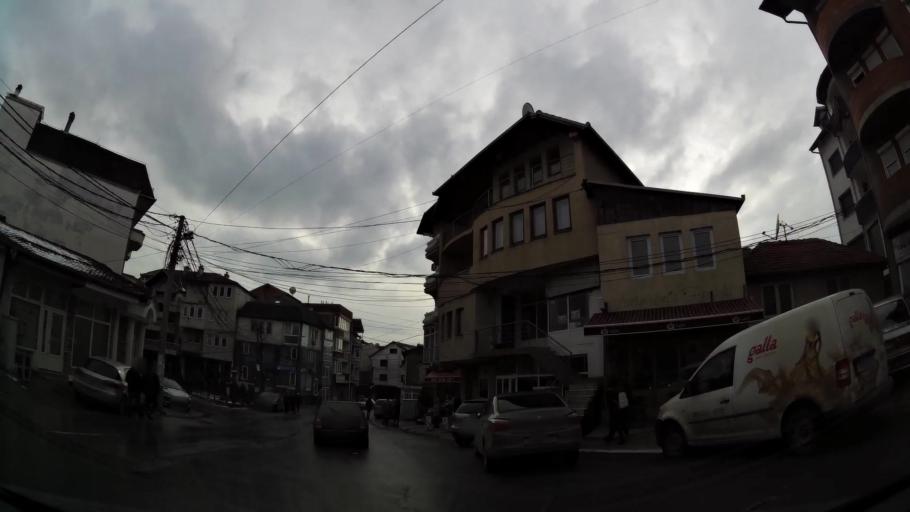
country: XK
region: Pristina
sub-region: Komuna e Prishtines
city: Pristina
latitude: 42.6736
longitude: 21.1661
